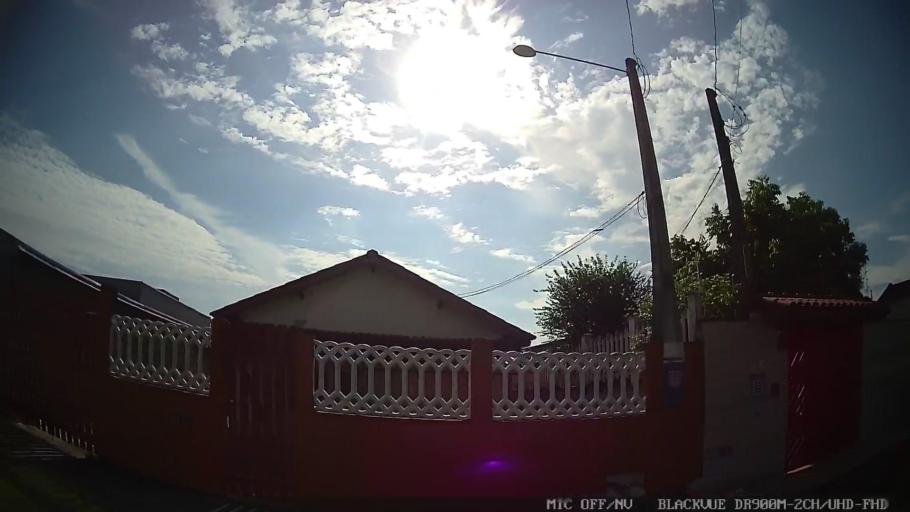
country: BR
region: Sao Paulo
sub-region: Caraguatatuba
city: Caraguatatuba
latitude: -23.6677
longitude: -45.4345
